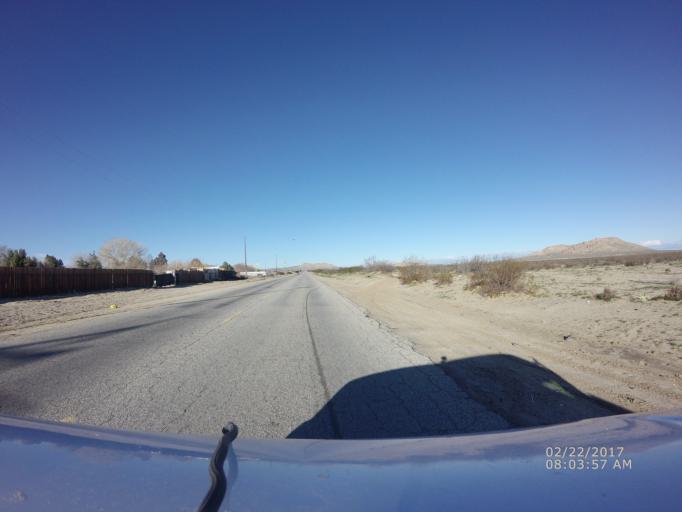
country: US
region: California
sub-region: Los Angeles County
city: Lake Los Angeles
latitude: 34.6316
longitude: -117.8278
